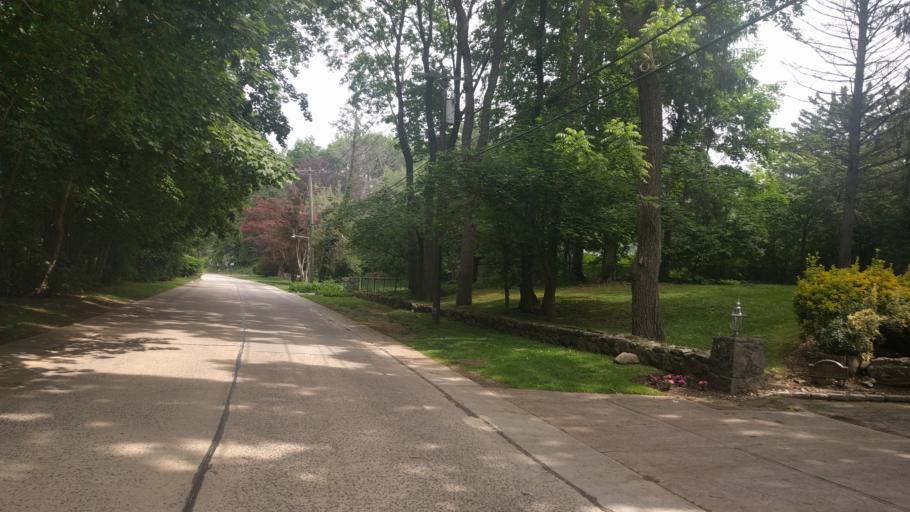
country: US
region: New York
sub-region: Nassau County
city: Roslyn Harbor
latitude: 40.8207
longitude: -73.6365
